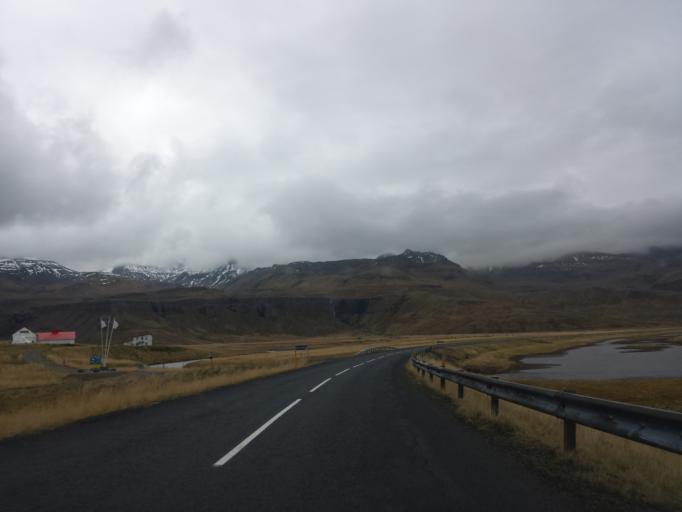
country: IS
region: West
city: Stykkisholmur
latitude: 64.9277
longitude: -23.2073
